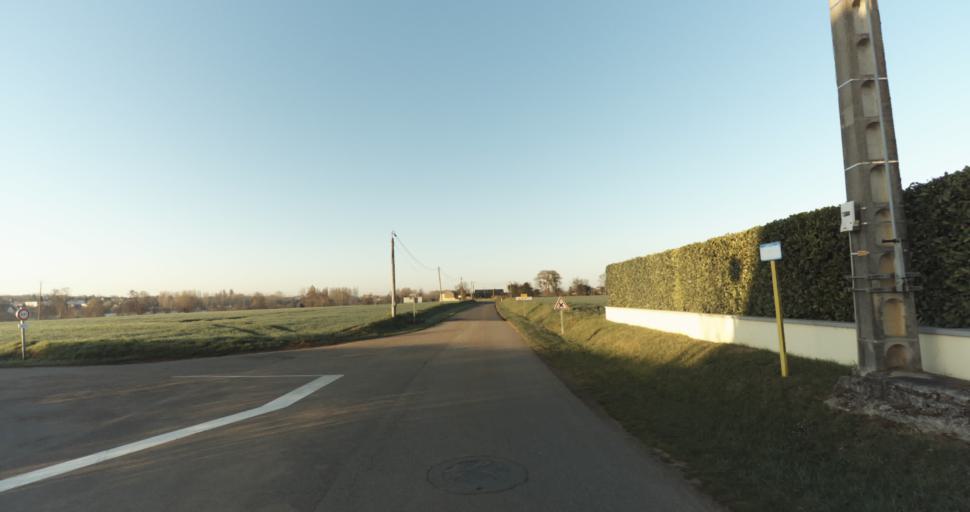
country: FR
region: Lower Normandy
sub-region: Departement du Calvados
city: Saint-Pierre-sur-Dives
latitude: 49.0322
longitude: -0.0297
